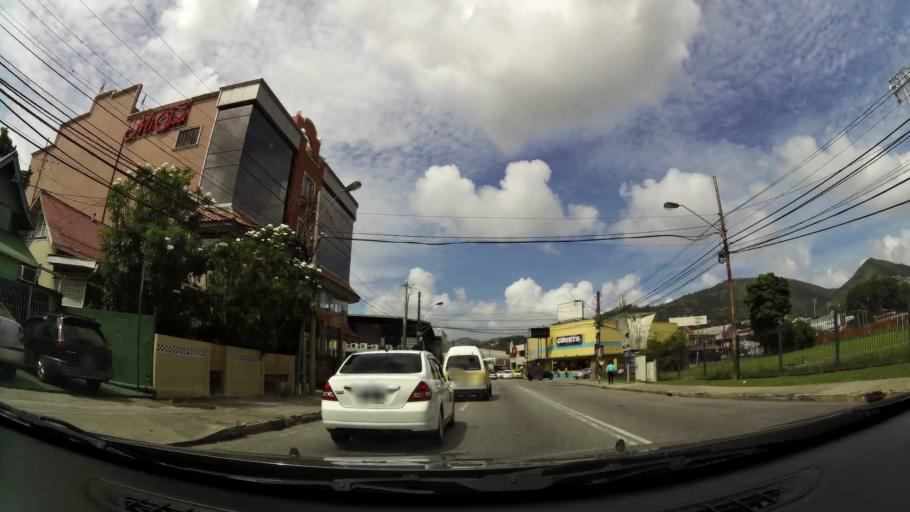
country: TT
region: City of Port of Spain
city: Port-of-Spain
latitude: 10.6702
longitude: -61.5291
